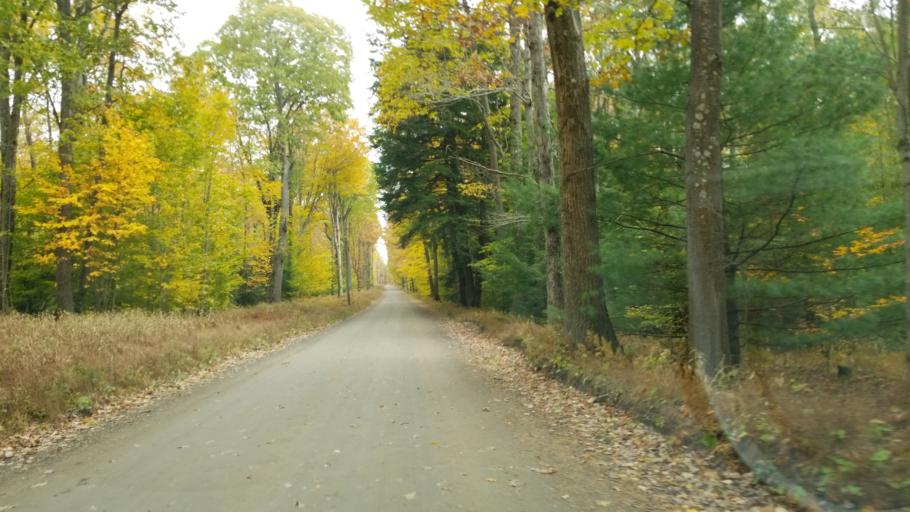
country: US
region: Pennsylvania
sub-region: Clearfield County
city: Shiloh
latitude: 41.1895
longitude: -78.3724
